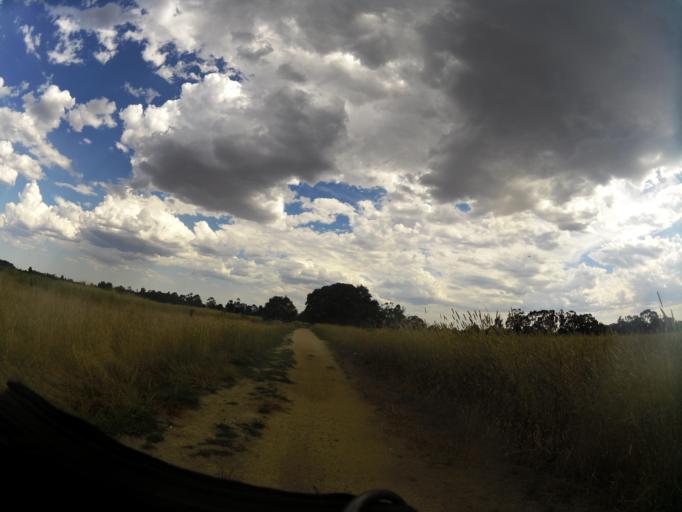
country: AU
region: Victoria
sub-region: Wellington
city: Heyfield
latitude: -38.0056
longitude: 146.6974
